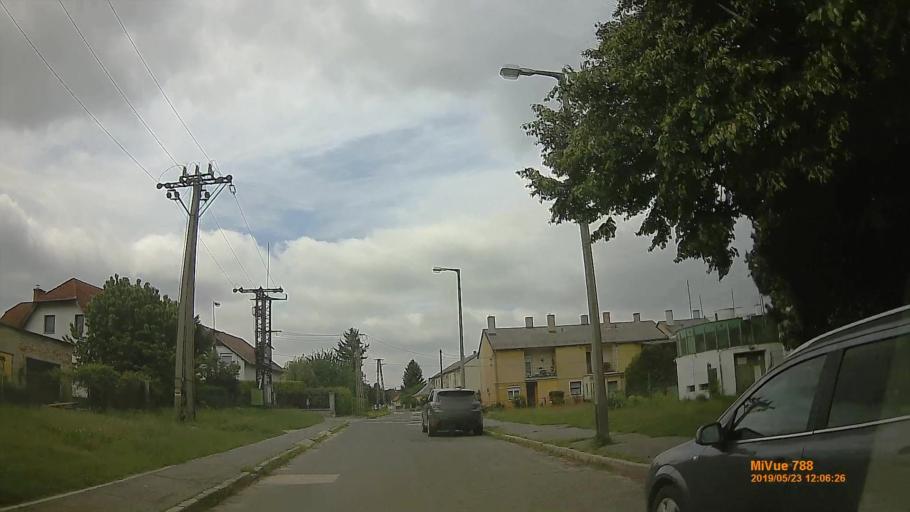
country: HU
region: Veszprem
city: Veszprem
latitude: 47.1030
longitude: 17.9178
